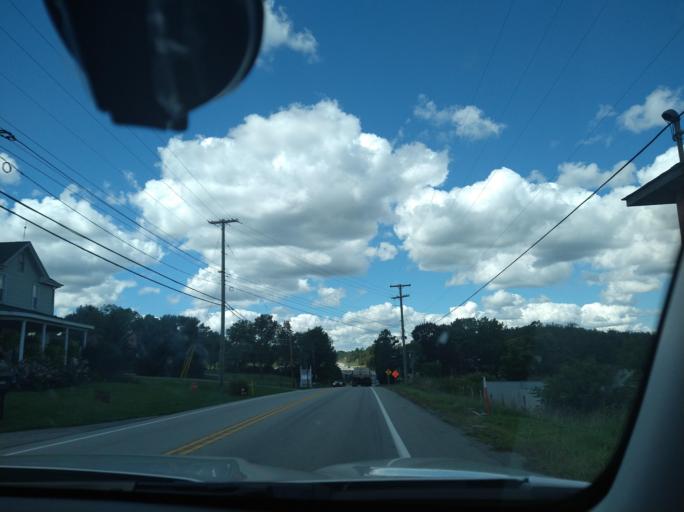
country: US
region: Pennsylvania
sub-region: Fayette County
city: Bear Rocks
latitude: 40.1051
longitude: -79.3726
